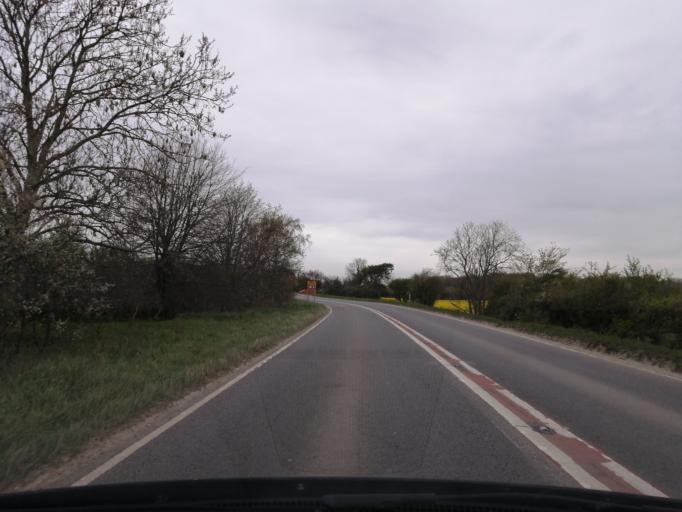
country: GB
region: England
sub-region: Peterborough
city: Wittering
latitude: 52.5885
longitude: -0.4435
